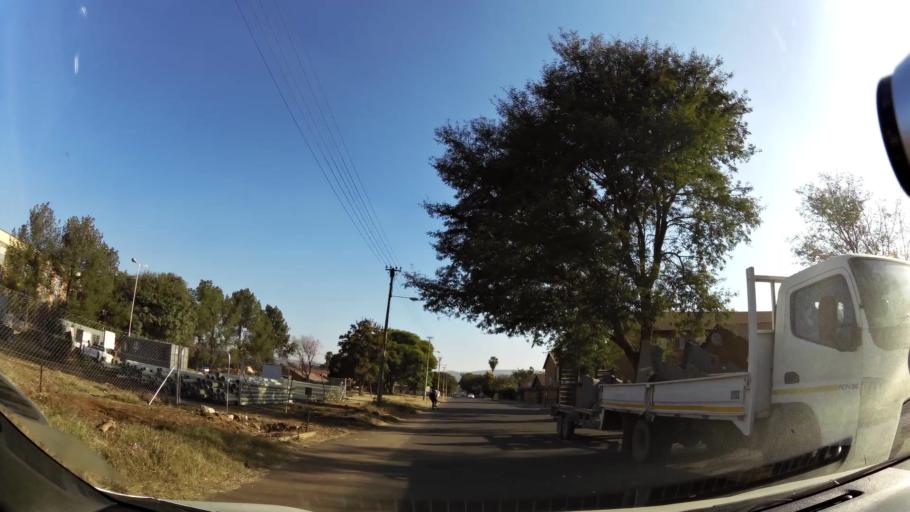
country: ZA
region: North-West
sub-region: Bojanala Platinum District Municipality
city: Rustenburg
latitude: -25.6658
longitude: 27.2492
